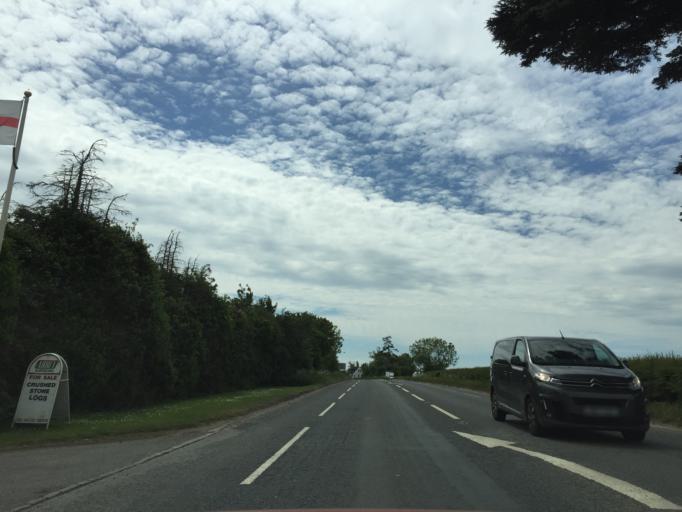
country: GB
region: England
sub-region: Gloucestershire
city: Stonehouse
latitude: 51.7935
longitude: -2.3072
